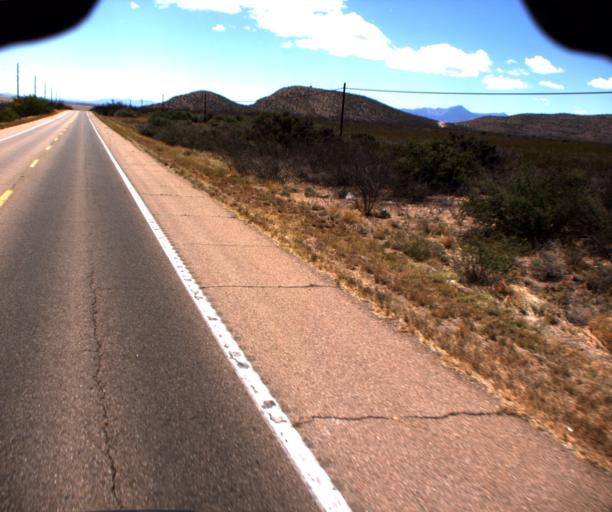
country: US
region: Arizona
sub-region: Cochise County
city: Naco
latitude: 31.3797
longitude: -109.9620
